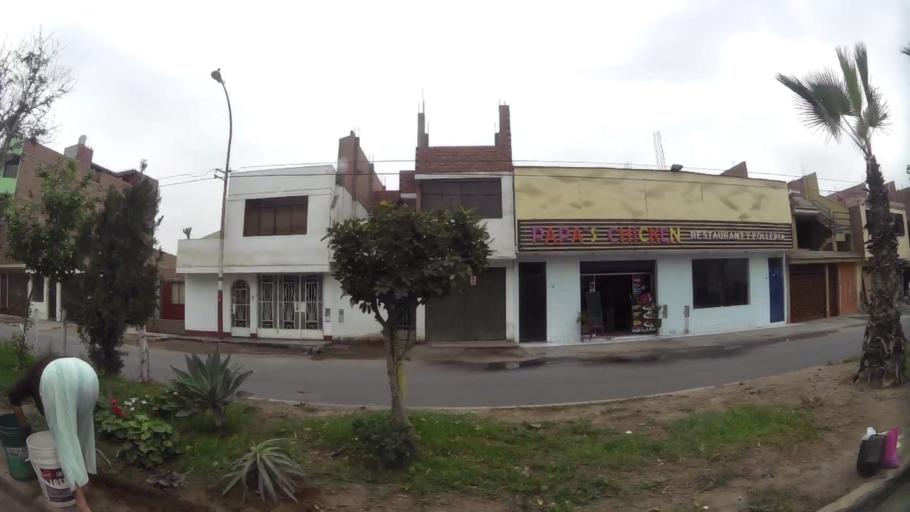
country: PE
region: Lima
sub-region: Lima
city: Independencia
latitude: -11.9469
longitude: -77.0902
